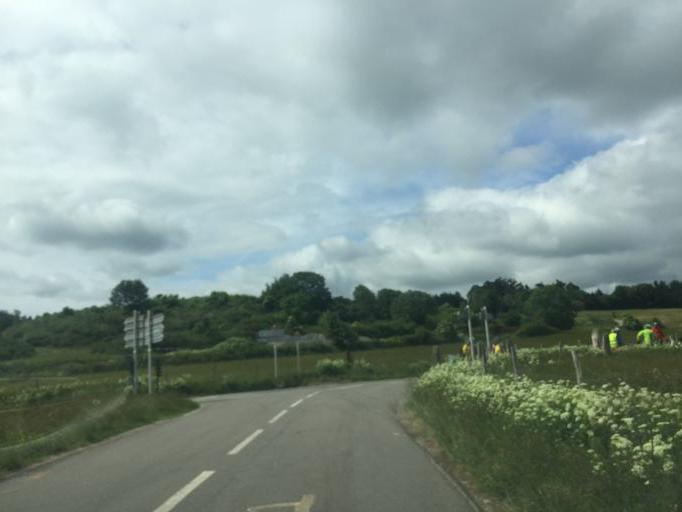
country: FR
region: Rhone-Alpes
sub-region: Departement de l'Ardeche
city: Saint-Priest
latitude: 44.6830
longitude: 4.5468
